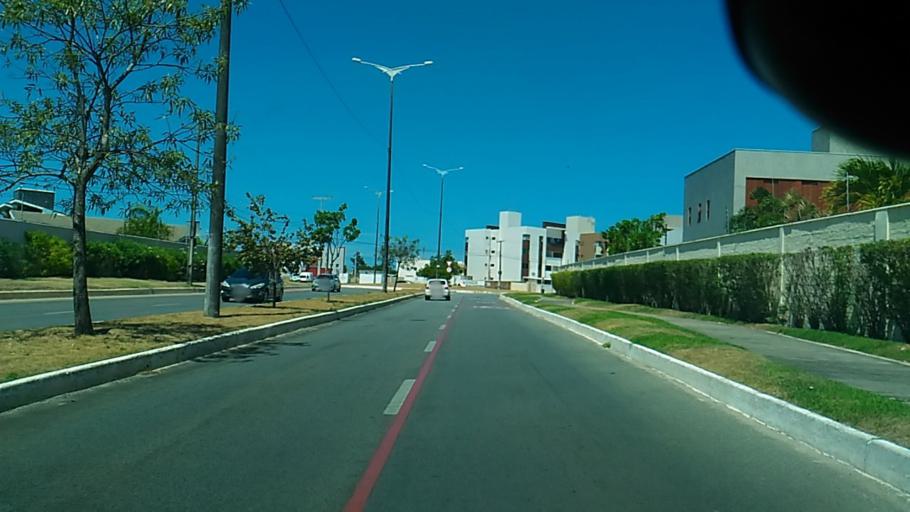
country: BR
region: Paraiba
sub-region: Joao Pessoa
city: Joao Pessoa
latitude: -7.1533
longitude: -34.8174
